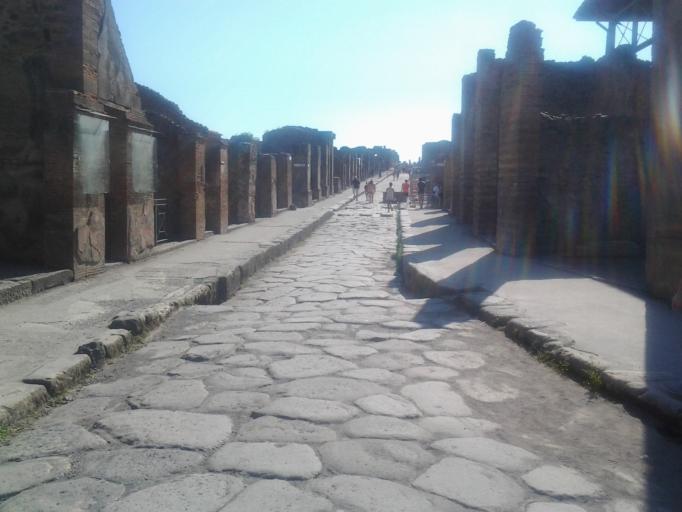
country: IT
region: Campania
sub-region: Provincia di Napoli
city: Pompei
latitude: 40.7497
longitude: 14.4877
